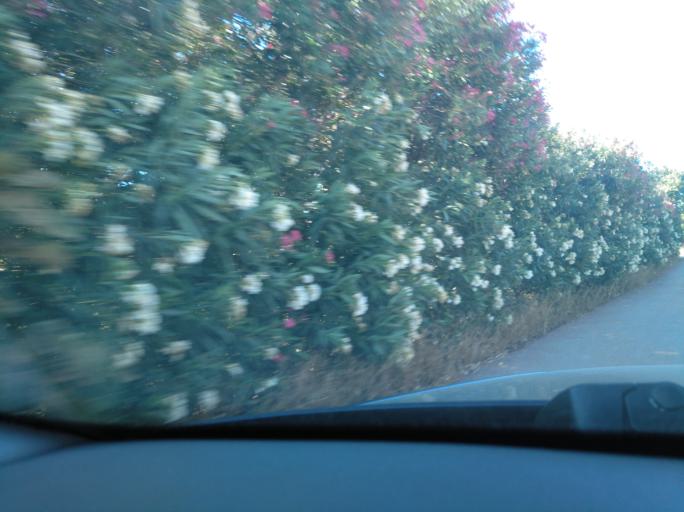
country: PT
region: Faro
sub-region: Vila Real de Santo Antonio
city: Monte Gordo
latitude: 37.1745
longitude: -7.5112
